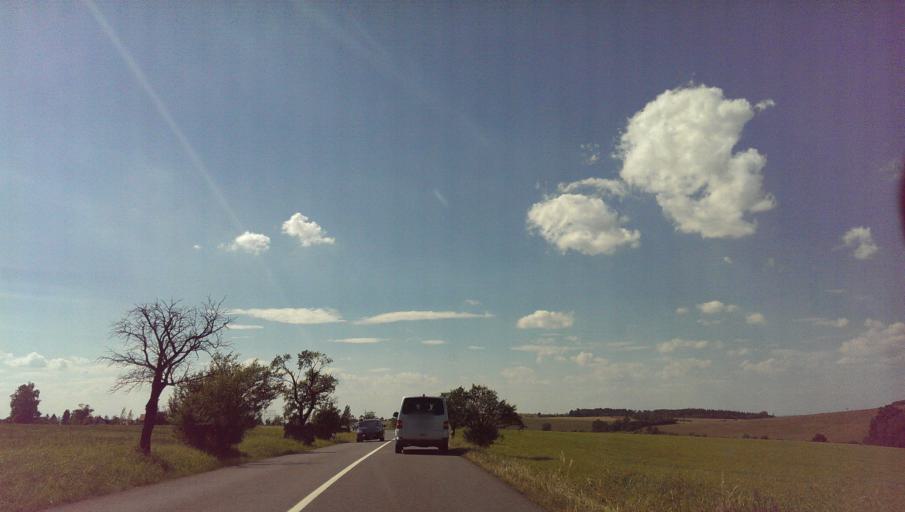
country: CZ
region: Zlin
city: Kelc
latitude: 49.4422
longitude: 17.8439
